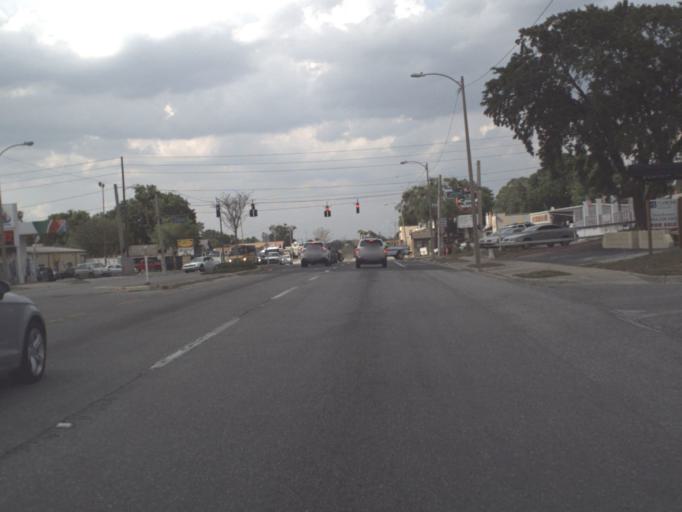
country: US
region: Florida
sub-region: Lake County
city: Eustis
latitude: 28.8409
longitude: -81.6854
